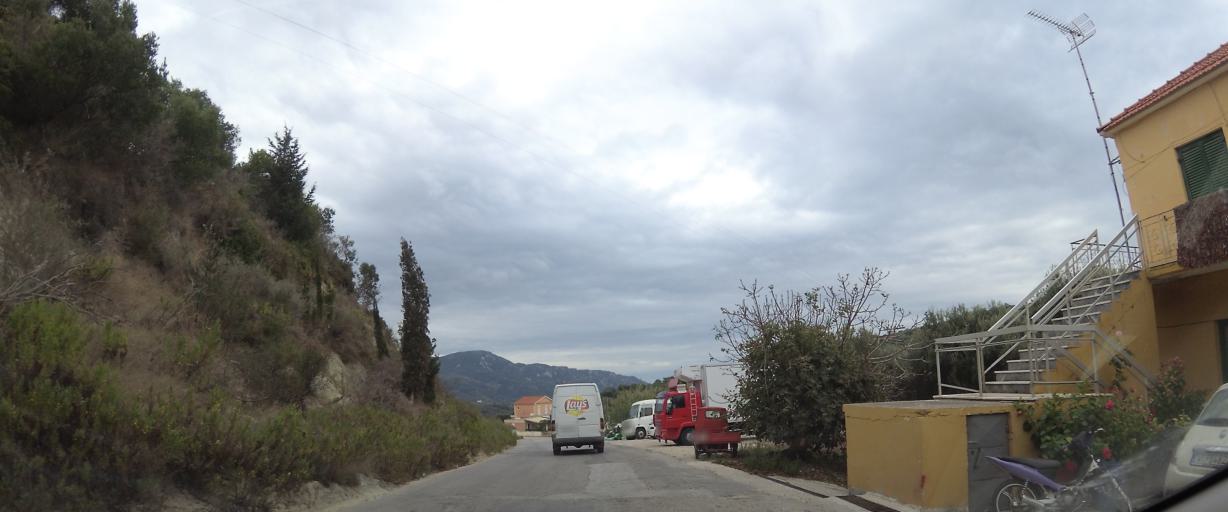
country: GR
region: Ionian Islands
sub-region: Nomos Kerkyras
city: Agios Georgis
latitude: 39.7388
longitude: 19.6742
